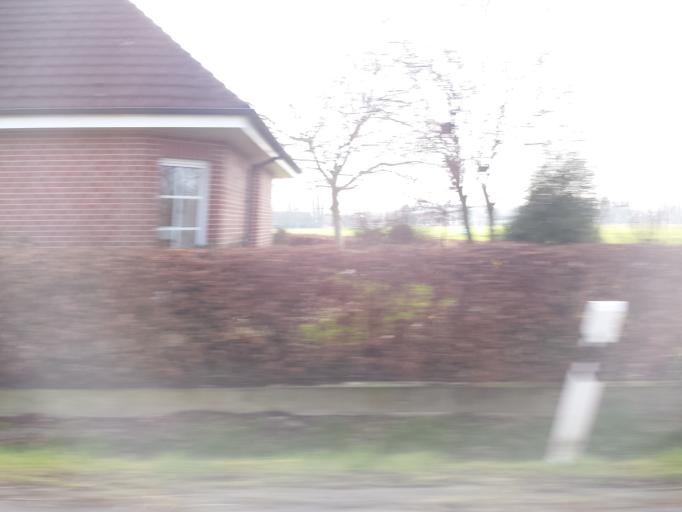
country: DE
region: North Rhine-Westphalia
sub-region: Regierungsbezirk Munster
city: Havixbeck
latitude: 51.9528
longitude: 7.5139
